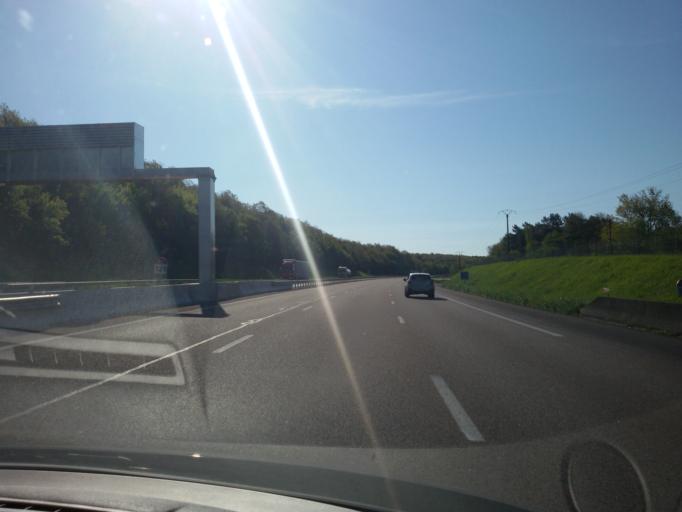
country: FR
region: Bourgogne
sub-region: Departement de l'Yonne
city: Aillant-sur-Tholon
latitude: 47.9257
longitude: 3.2756
